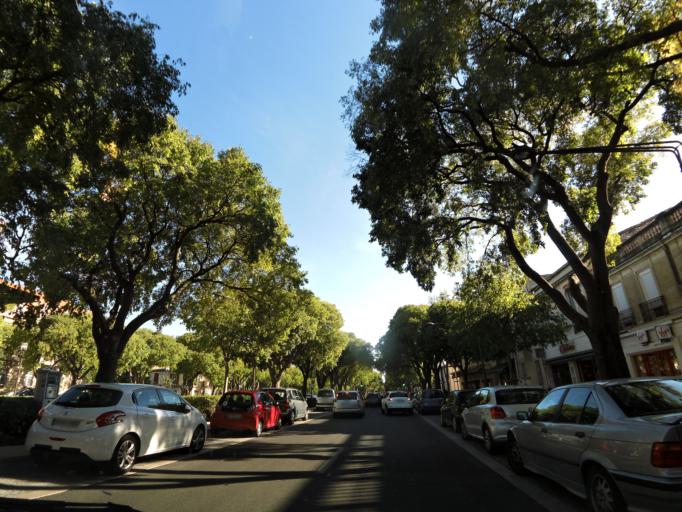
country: FR
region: Languedoc-Roussillon
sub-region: Departement du Gard
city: Nimes
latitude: 43.8352
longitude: 4.3507
